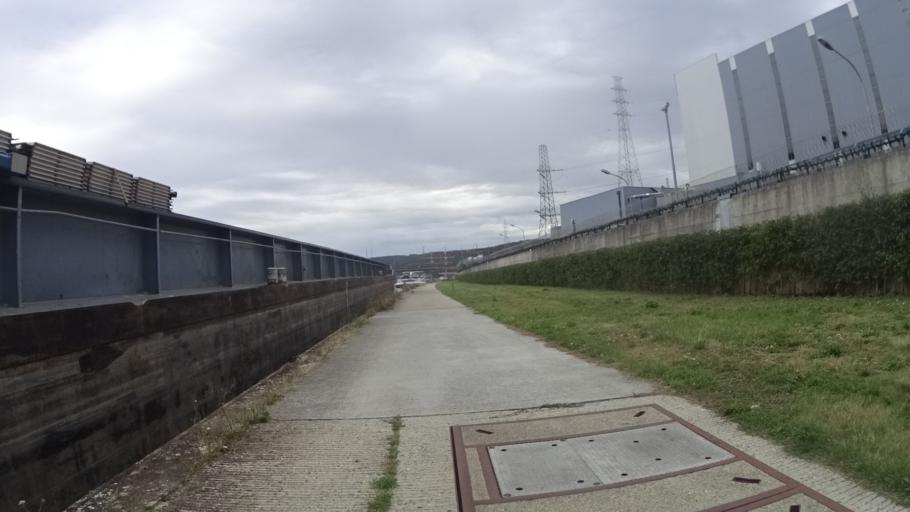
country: BE
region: Wallonia
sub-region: Province de Liege
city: Amay
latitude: 50.5359
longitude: 5.2786
